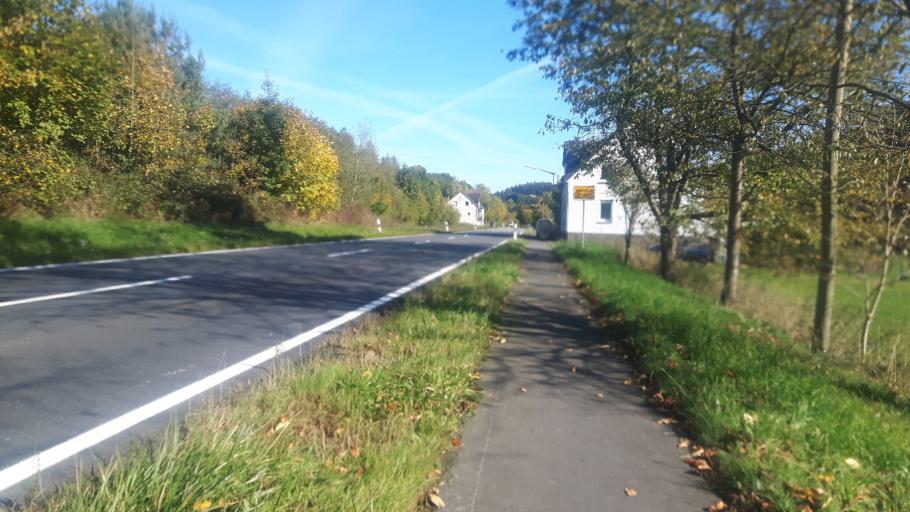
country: DE
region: Rheinland-Pfalz
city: Wissen
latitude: 50.7893
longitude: 7.7563
